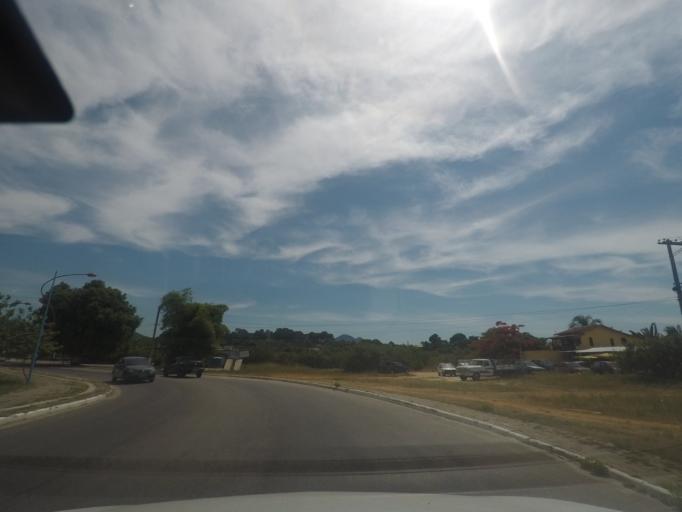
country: BR
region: Rio de Janeiro
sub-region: Marica
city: Marica
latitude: -22.9459
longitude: -42.7522
